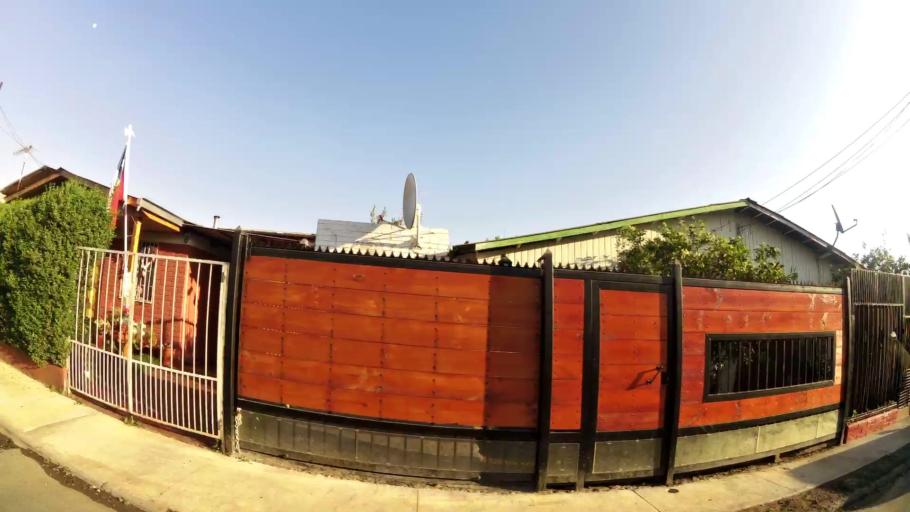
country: CL
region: Santiago Metropolitan
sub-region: Provincia de Santiago
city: La Pintana
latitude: -33.5489
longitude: -70.6228
